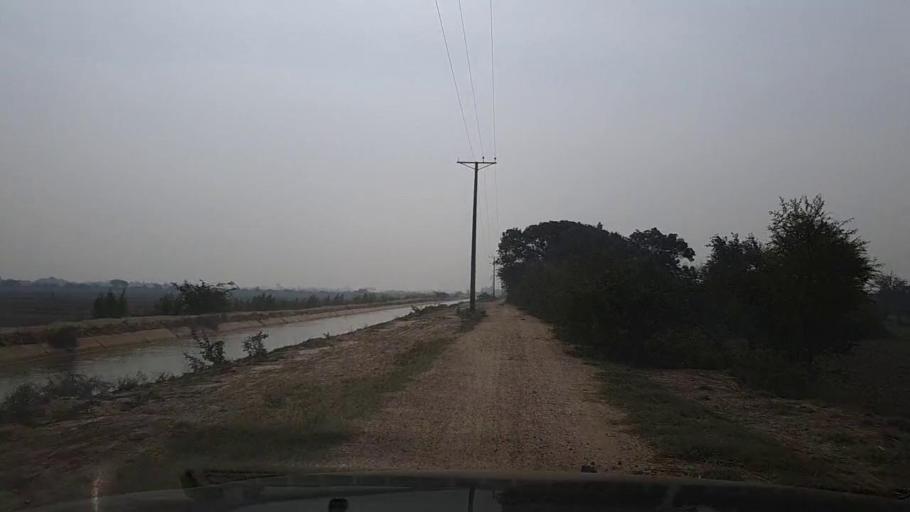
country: PK
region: Sindh
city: Mirpur Sakro
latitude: 24.5323
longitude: 67.8116
